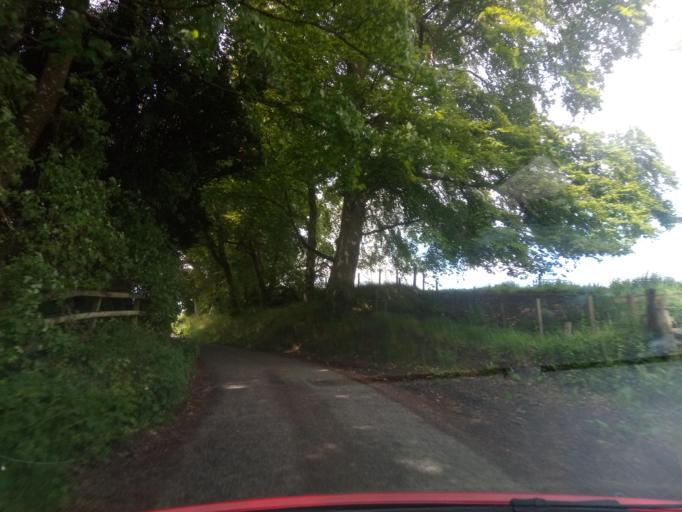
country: GB
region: Scotland
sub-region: The Scottish Borders
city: Selkirk
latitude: 55.5286
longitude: -2.8675
